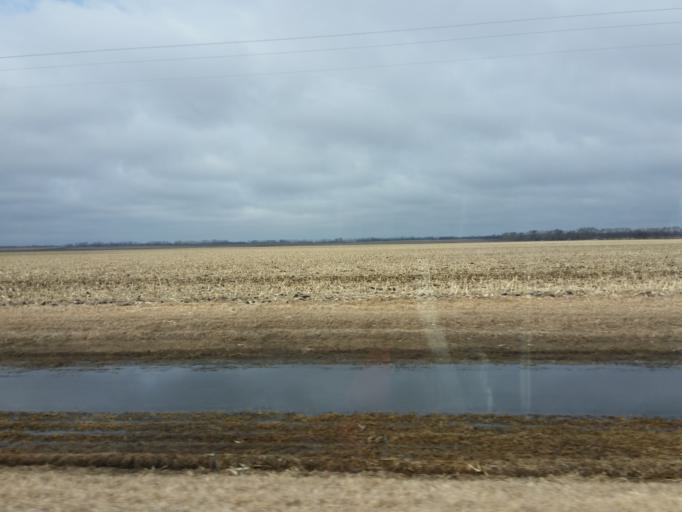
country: US
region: North Dakota
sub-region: Traill County
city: Mayville
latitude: 47.3874
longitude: -97.3264
